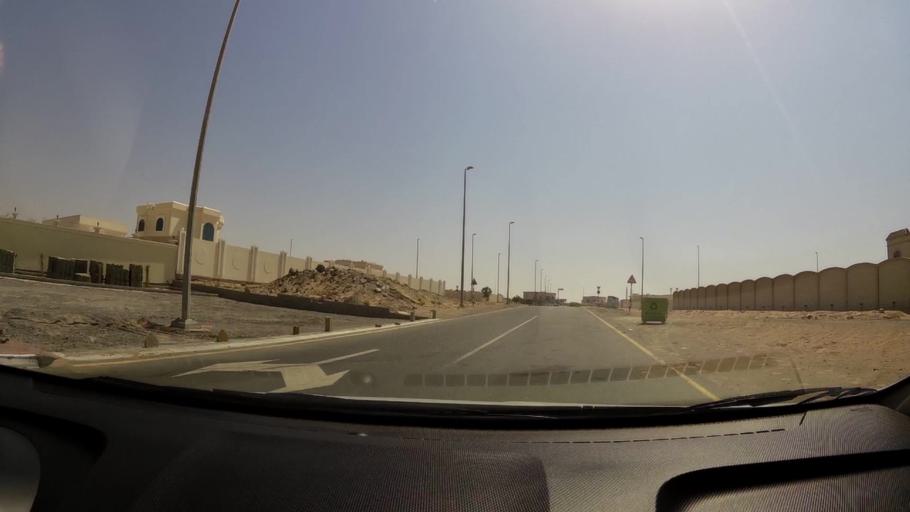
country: AE
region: Umm al Qaywayn
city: Umm al Qaywayn
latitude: 25.4875
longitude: 55.6040
